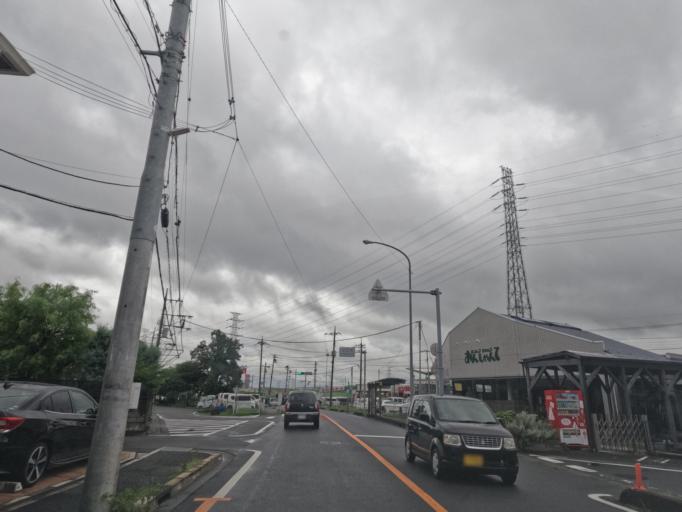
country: JP
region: Saitama
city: Shimotoda
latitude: 35.8479
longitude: 139.6895
